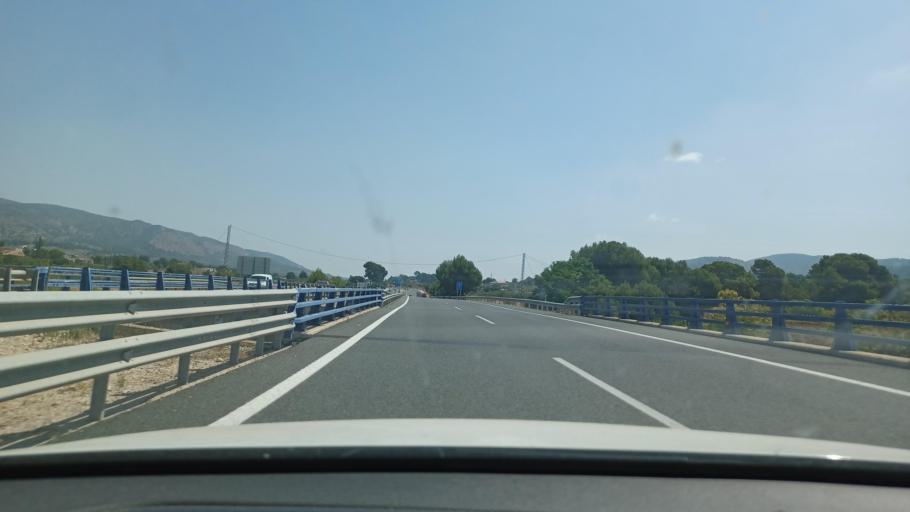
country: ES
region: Valencia
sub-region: Provincia de Alicante
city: Ibi
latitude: 38.6086
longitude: -0.5793
